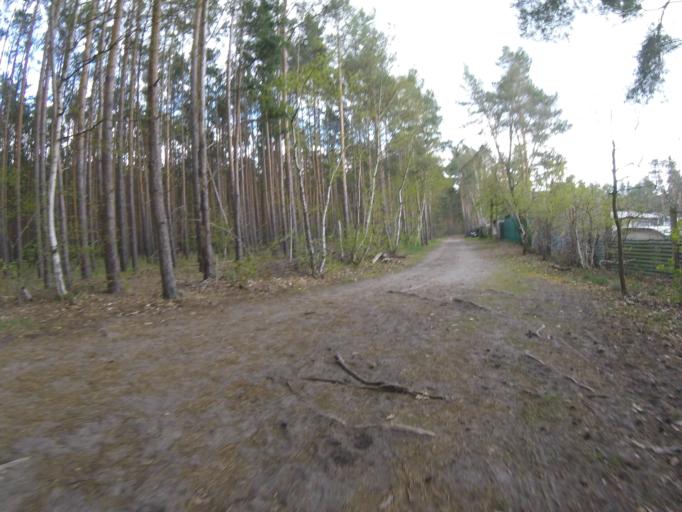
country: DE
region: Brandenburg
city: Bestensee
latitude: 52.2574
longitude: 13.6719
